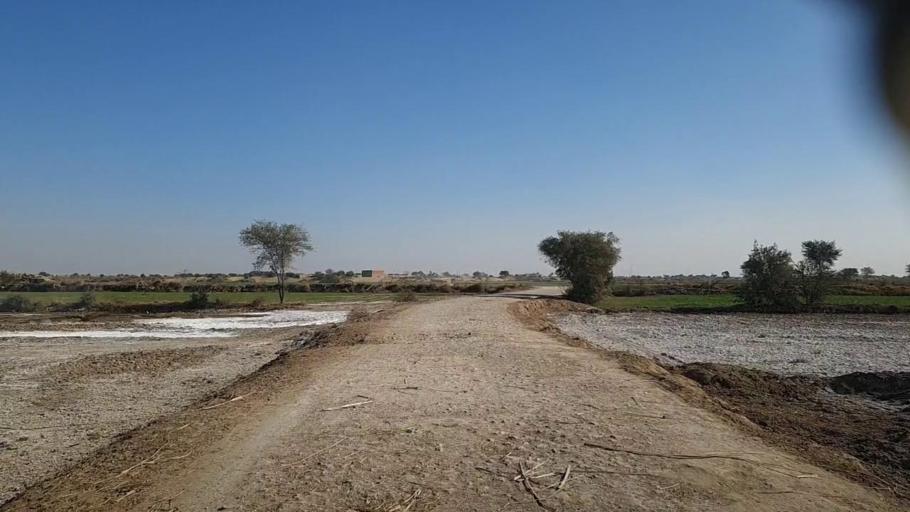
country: PK
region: Sindh
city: Khairpur
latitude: 27.9253
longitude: 69.7362
